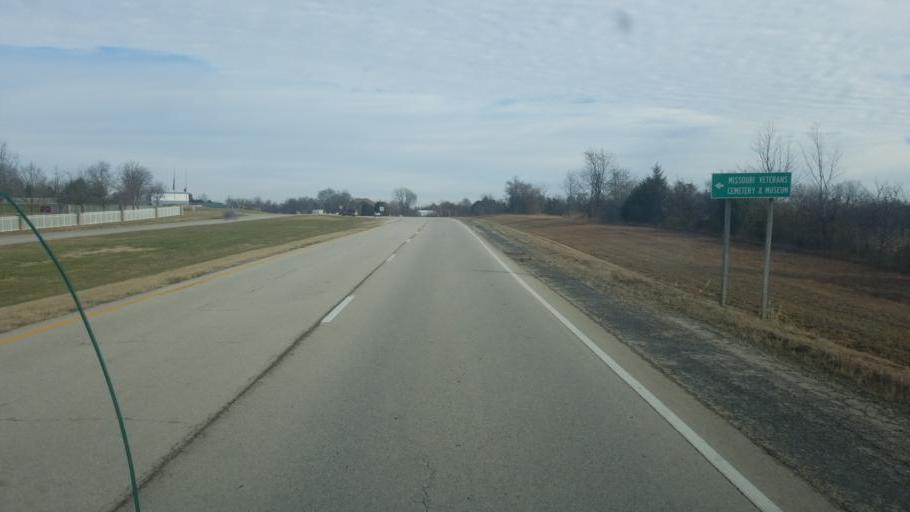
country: US
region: Missouri
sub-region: Stoddard County
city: Bloomfield
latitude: 36.8626
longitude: -89.9323
